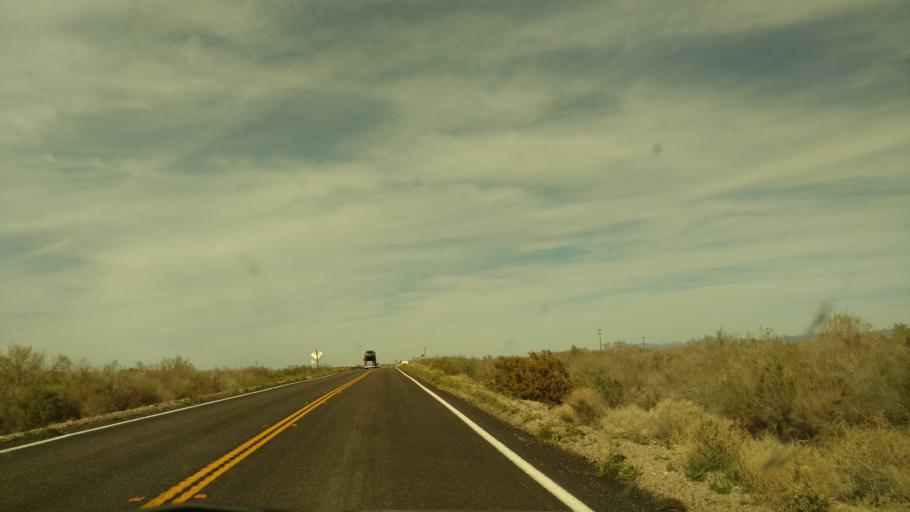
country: US
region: California
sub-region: Riverside County
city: Mesa Verde
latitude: 33.3597
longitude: -114.7242
